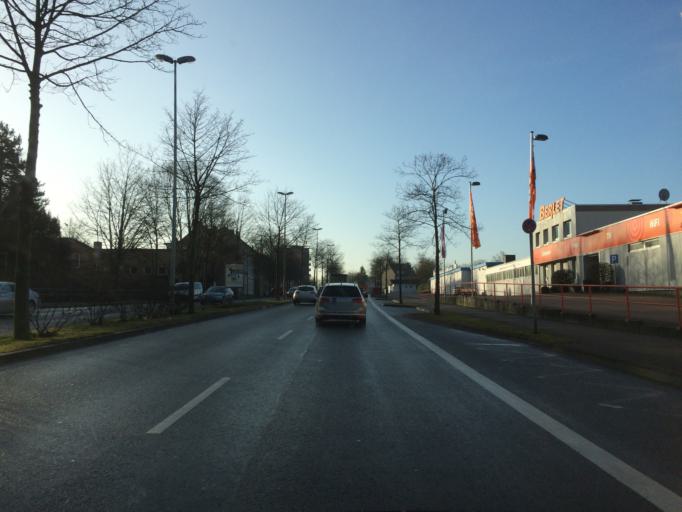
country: DE
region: North Rhine-Westphalia
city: Bochum-Hordel
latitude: 51.5332
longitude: 7.1858
